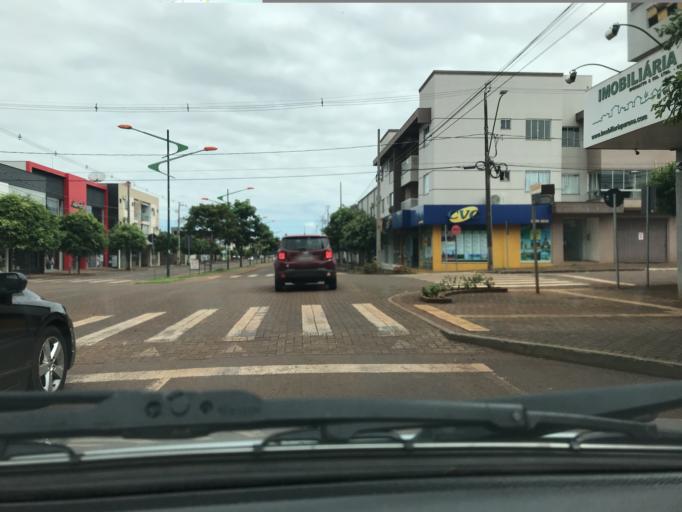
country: BR
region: Parana
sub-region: Palotina
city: Palotina
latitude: -24.2813
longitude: -53.8405
